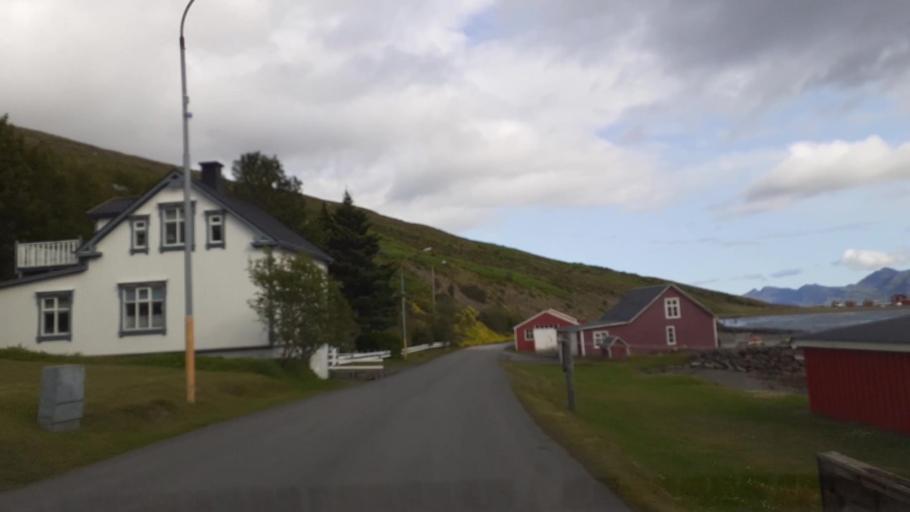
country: IS
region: East
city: Eskifjoerdur
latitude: 65.0646
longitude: -13.9991
